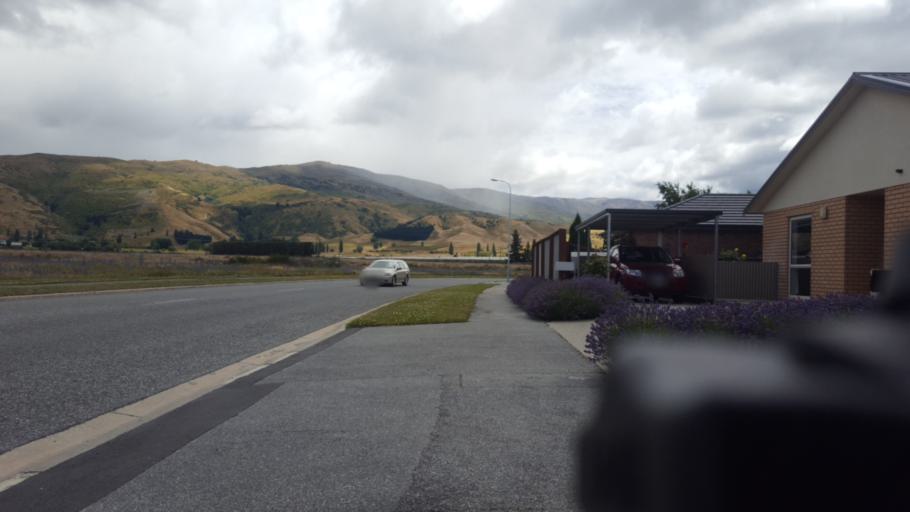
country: NZ
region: Otago
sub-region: Queenstown-Lakes District
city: Wanaka
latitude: -45.0441
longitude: 169.1802
